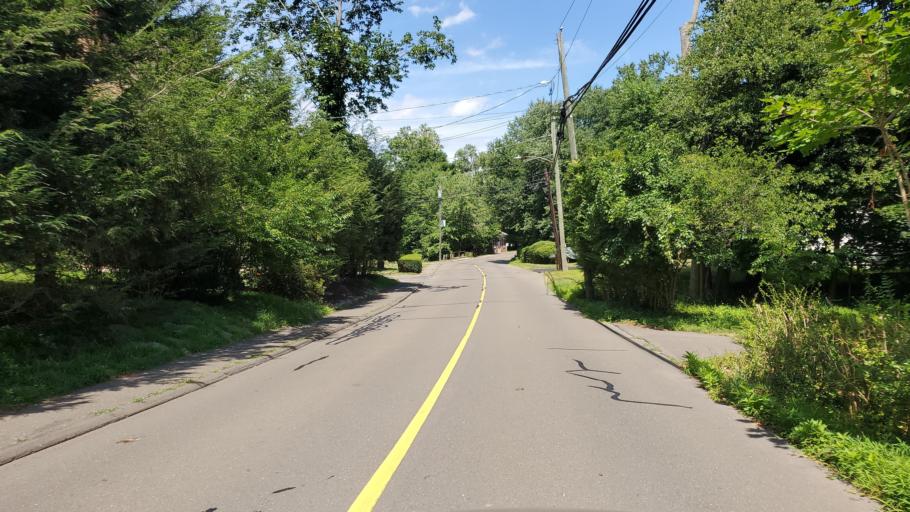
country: US
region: Connecticut
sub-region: Fairfield County
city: Westport
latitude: 41.1322
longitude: -73.3295
